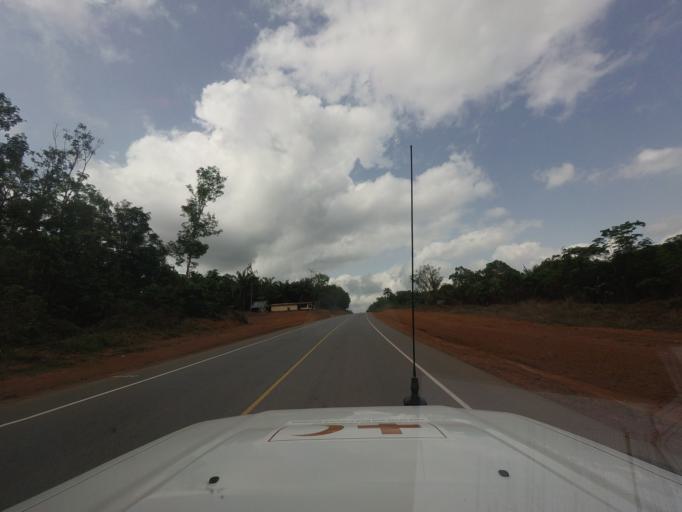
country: LR
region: Nimba
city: Sanniquellie
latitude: 7.2063
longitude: -9.0146
